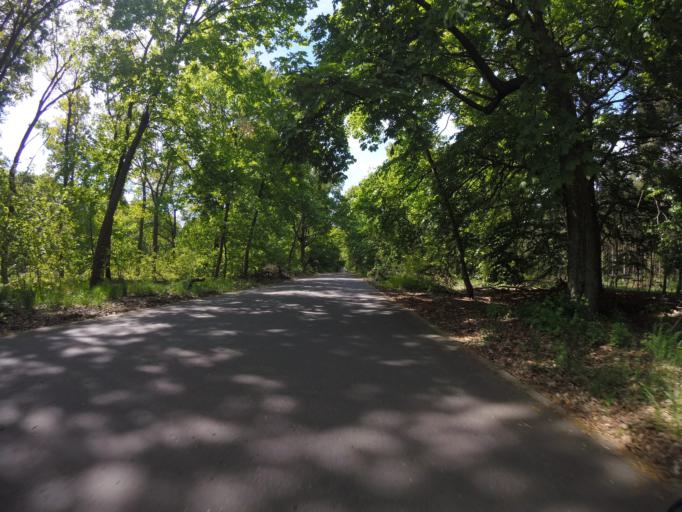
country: DE
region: Berlin
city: Nikolassee
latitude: 52.4483
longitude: 13.2092
